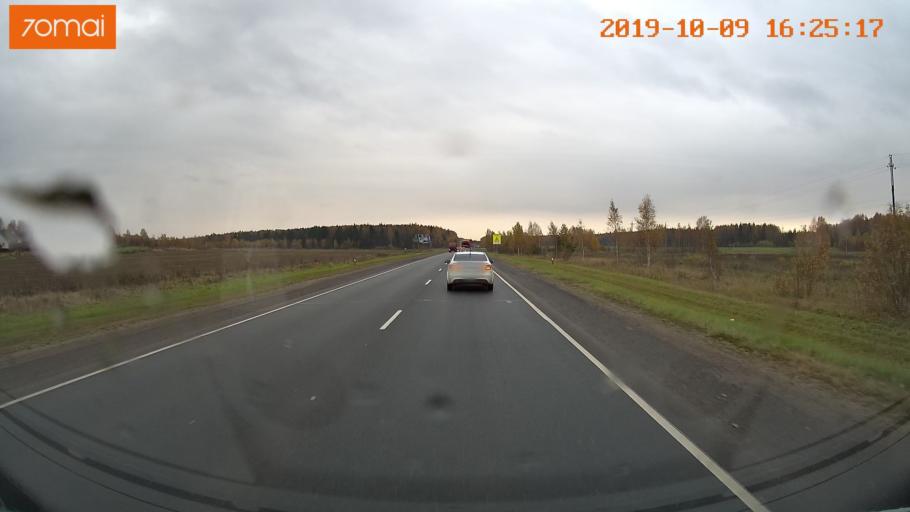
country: RU
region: Kostroma
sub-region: Kostromskoy Rayon
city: Kostroma
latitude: 57.6437
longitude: 40.9185
